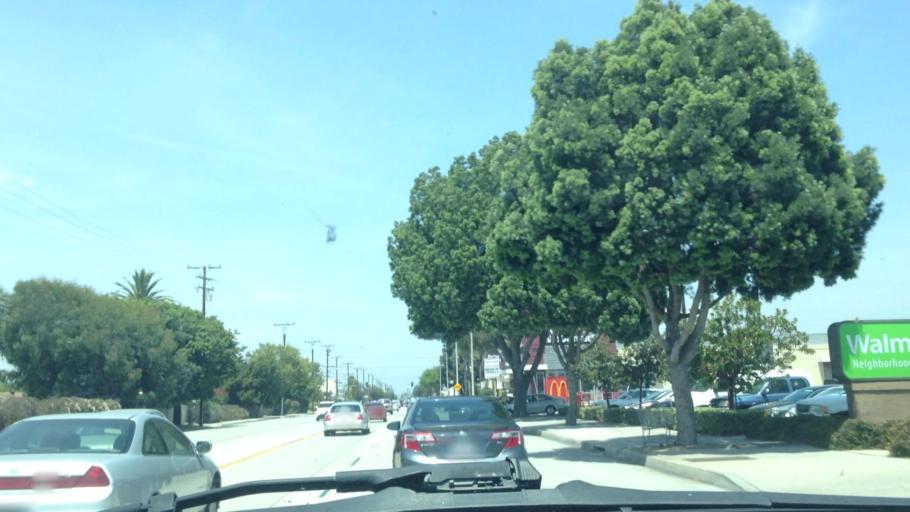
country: US
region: California
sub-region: Los Angeles County
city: Downey
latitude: 33.9283
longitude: -118.1487
